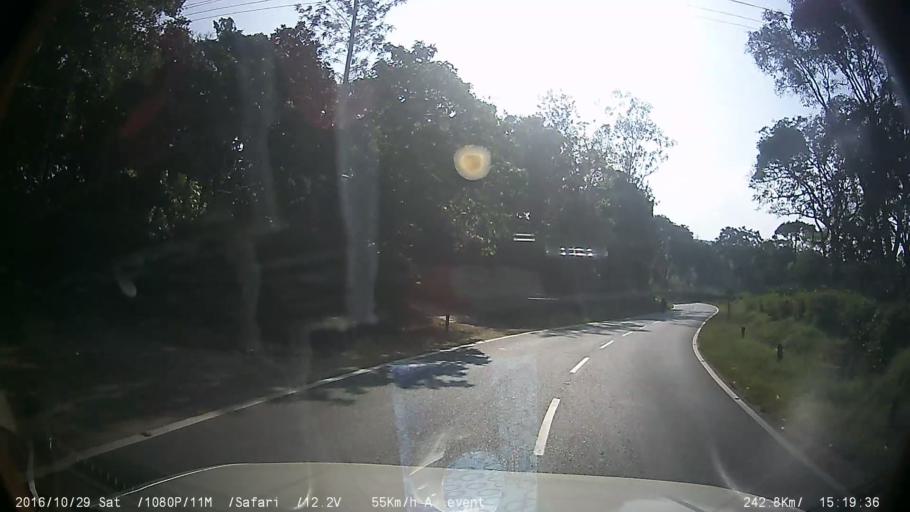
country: IN
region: Karnataka
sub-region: Kodagu
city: Suntikoppa
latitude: 12.4348
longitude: 75.7872
